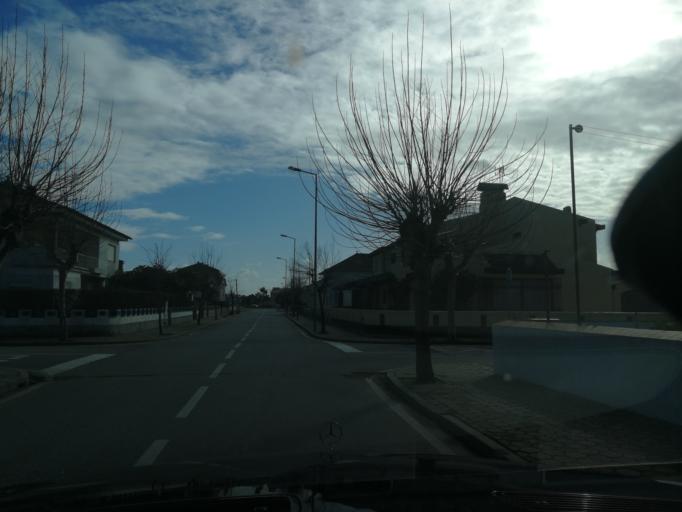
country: PT
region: Aveiro
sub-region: Murtosa
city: Murtosa
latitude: 40.7601
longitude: -8.7087
